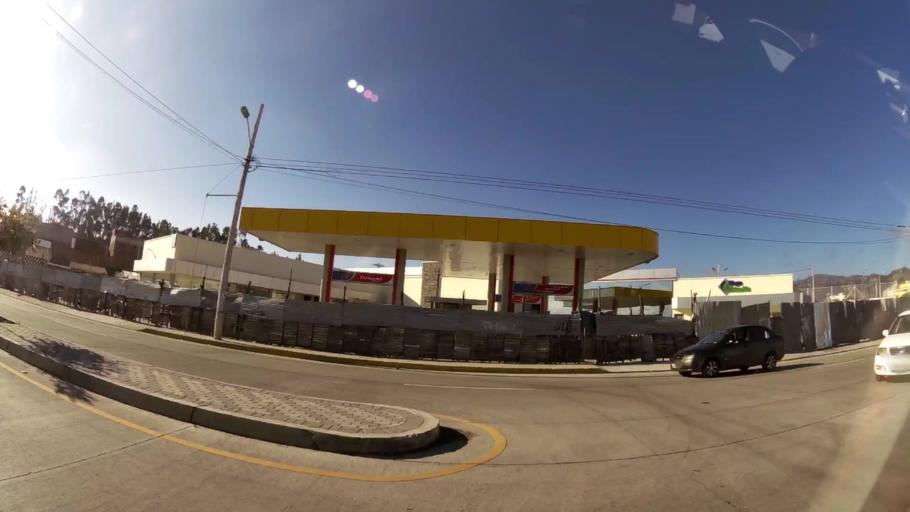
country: EC
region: Chimborazo
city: Riobamba
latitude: -1.6857
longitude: -78.6459
